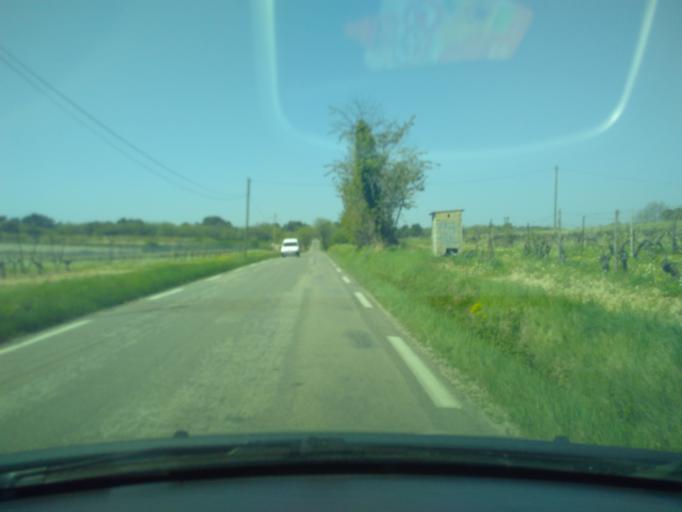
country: FR
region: Provence-Alpes-Cote d'Azur
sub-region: Departement du Vaucluse
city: Malemort-du-Comtat
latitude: 44.0233
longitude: 5.1443
